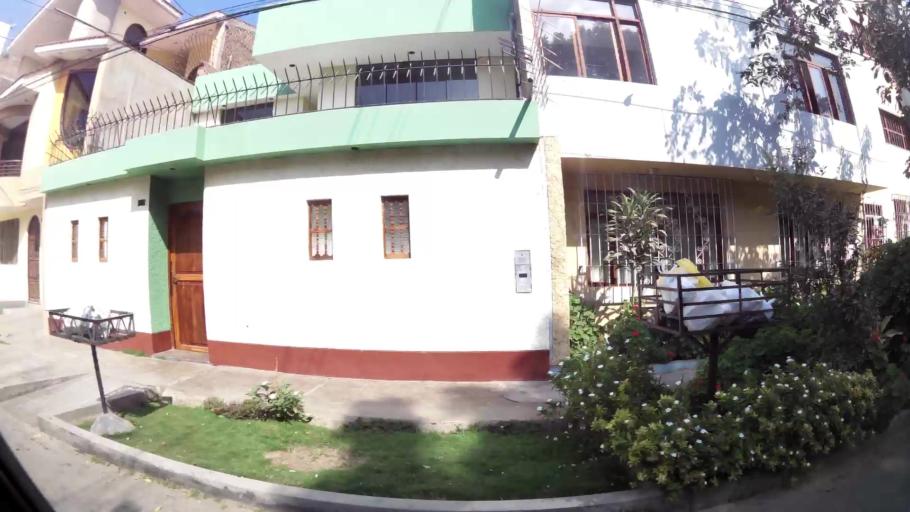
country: PE
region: La Libertad
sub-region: Provincia de Trujillo
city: Trujillo
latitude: -8.1239
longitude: -79.0192
